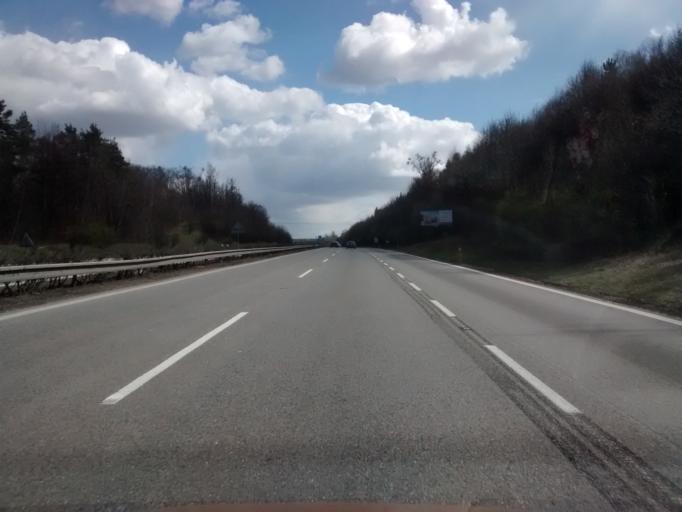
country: CZ
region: Central Bohemia
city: Odolena Voda
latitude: 50.2301
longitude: 14.3992
